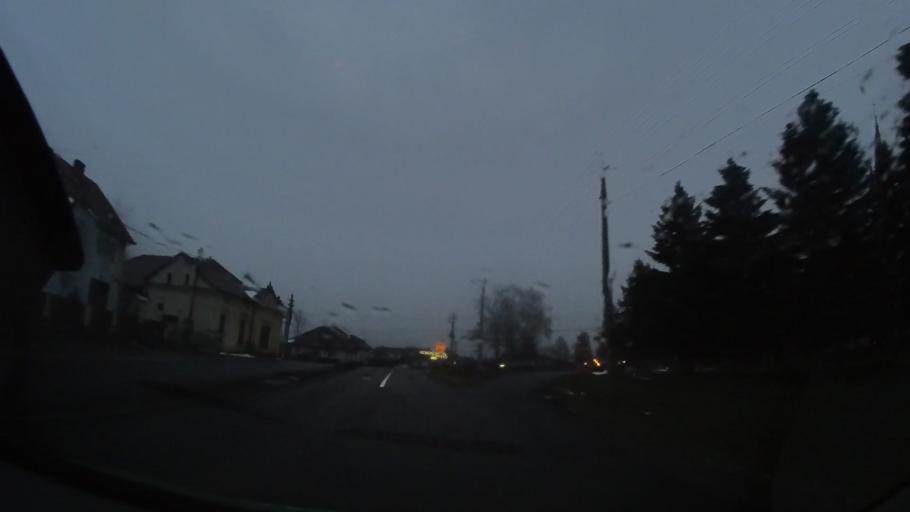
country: RO
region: Harghita
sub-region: Comuna Ditrau
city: Ditrau
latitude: 46.8042
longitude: 25.4945
